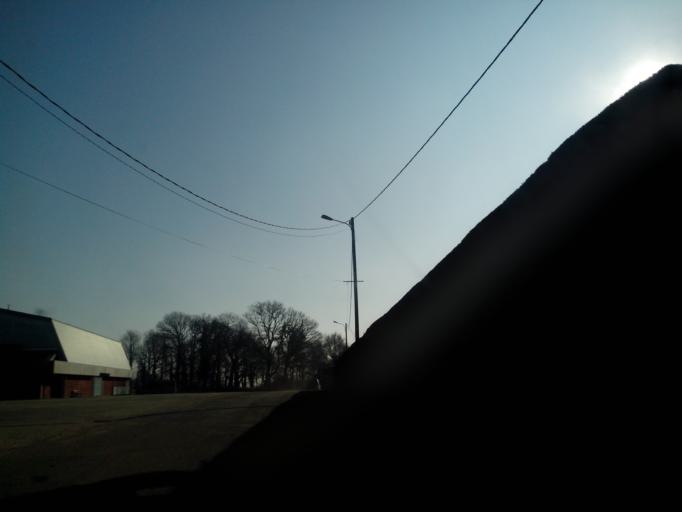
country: FR
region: Brittany
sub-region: Departement du Morbihan
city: Meneac
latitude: 48.1366
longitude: -2.4528
